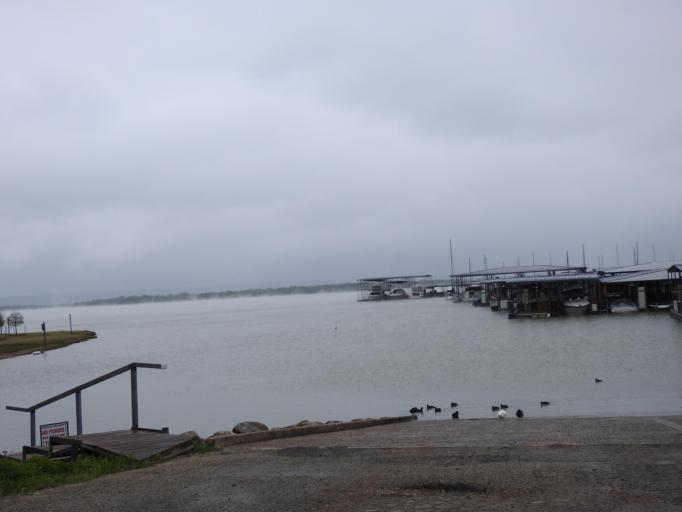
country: US
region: Texas
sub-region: Dallas County
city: Cedar Hill
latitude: 32.6311
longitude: -97.0397
